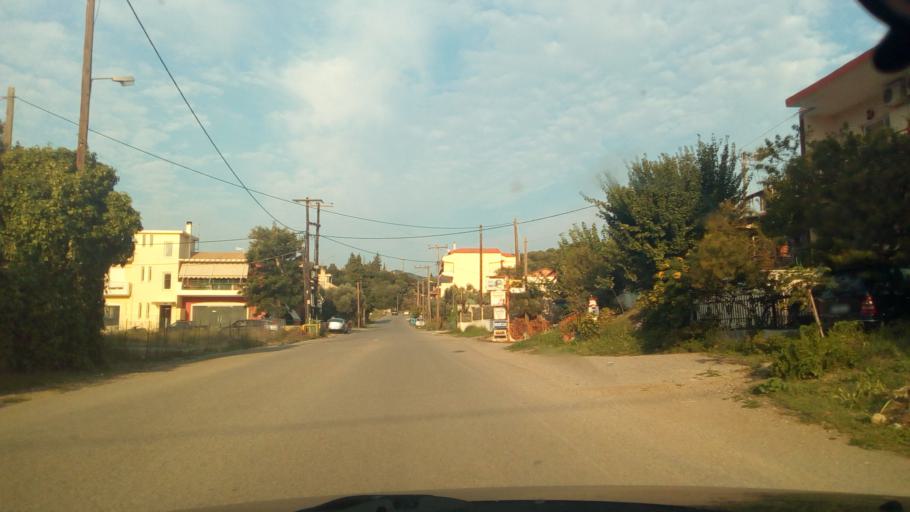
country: GR
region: West Greece
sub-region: Nomos Aitolias kai Akarnanias
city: Nafpaktos
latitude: 38.3935
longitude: 21.8157
